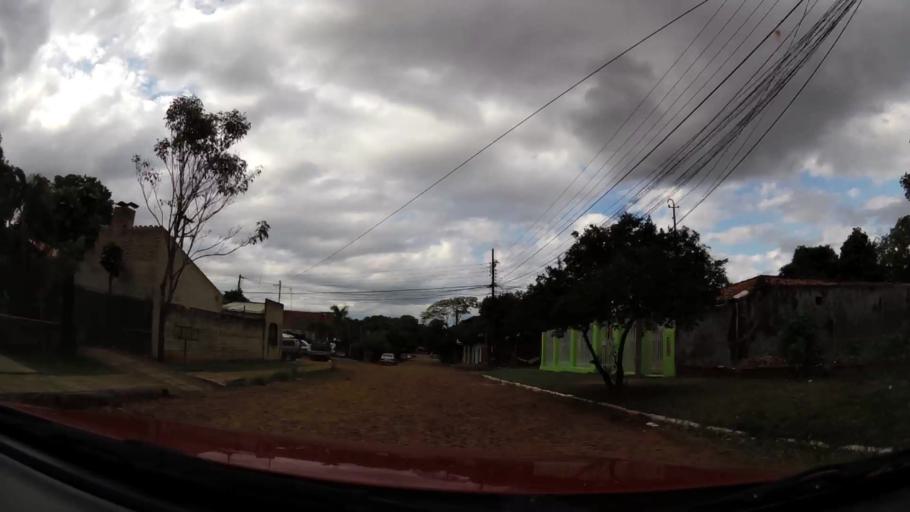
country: PY
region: Central
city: San Lorenzo
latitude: -25.2829
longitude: -57.4980
